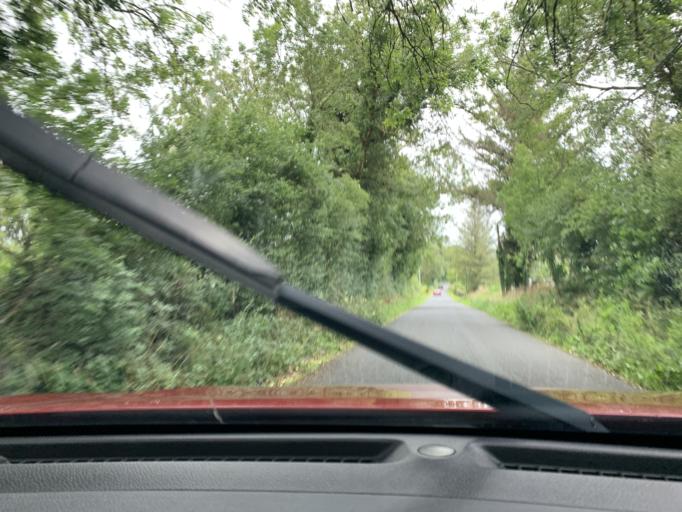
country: IE
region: Connaught
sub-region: County Leitrim
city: Carrick-on-Shannon
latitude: 53.8650
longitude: -8.1367
